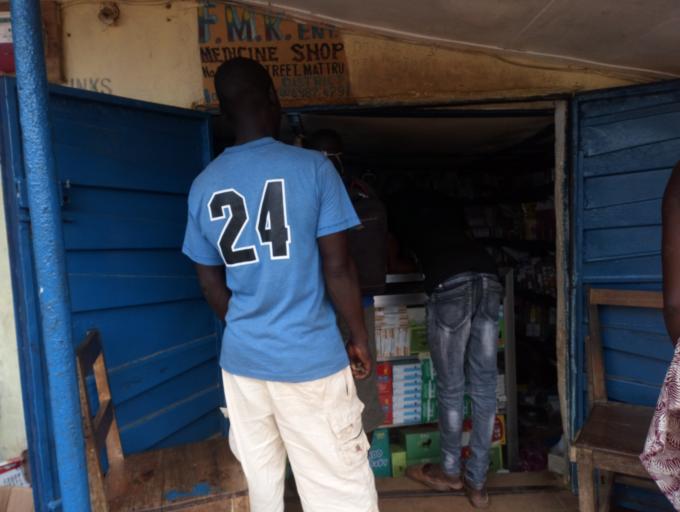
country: SL
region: Southern Province
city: Mogbwemo
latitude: 7.6054
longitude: -12.1787
